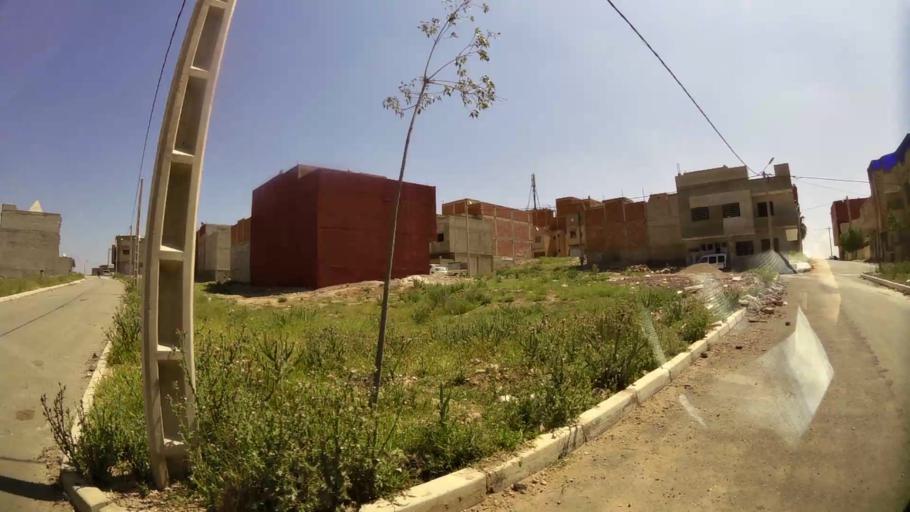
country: MA
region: Oriental
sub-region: Oujda-Angad
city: Oujda
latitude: 34.6723
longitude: -1.9468
